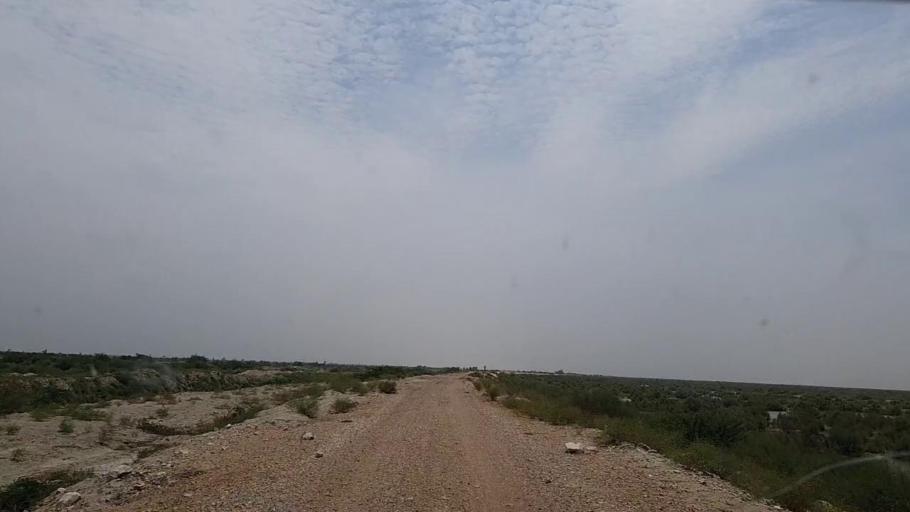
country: PK
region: Sindh
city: Phulji
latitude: 26.8691
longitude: 67.6468
